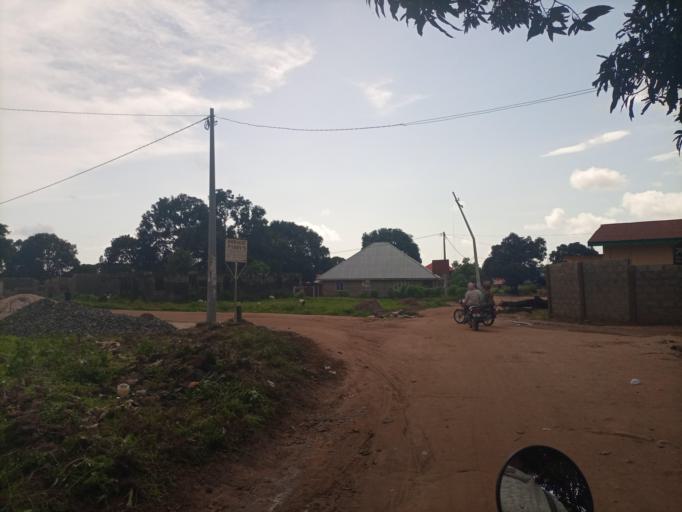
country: SL
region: Northern Province
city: Masoyila
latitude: 8.6055
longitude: -13.1759
